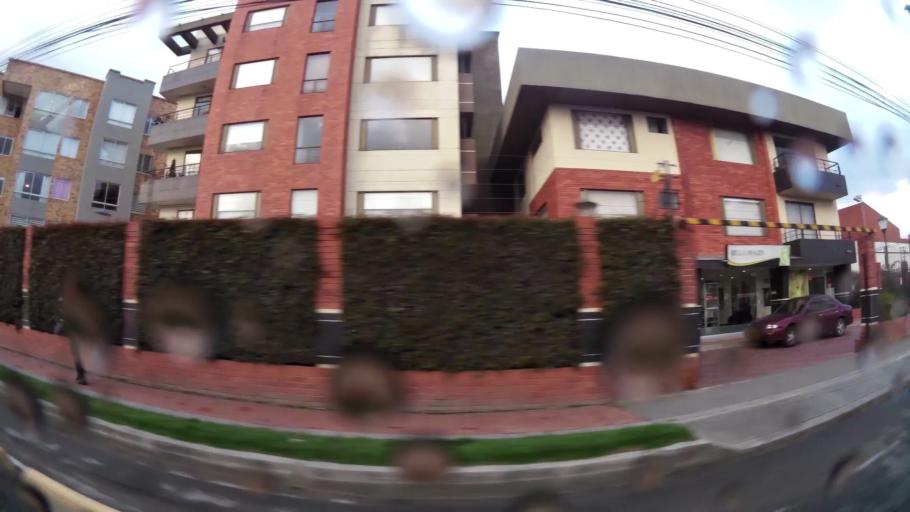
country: CO
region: Cundinamarca
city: Chia
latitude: 4.8663
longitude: -74.0489
